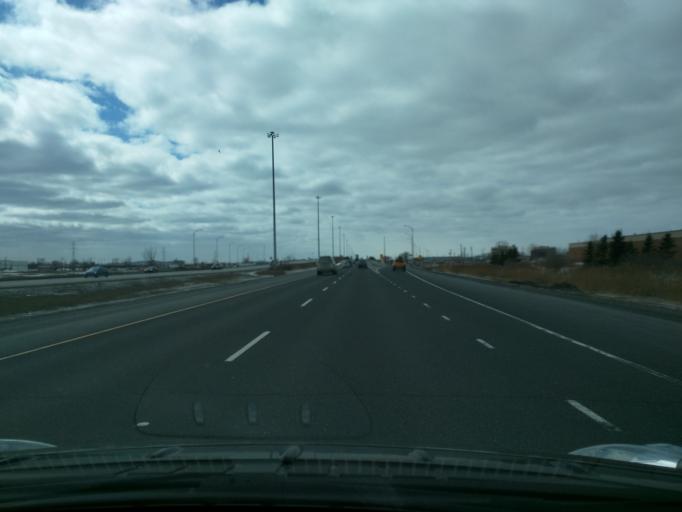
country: CA
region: Quebec
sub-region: Monteregie
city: Boucherville
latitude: 45.5702
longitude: -73.4031
